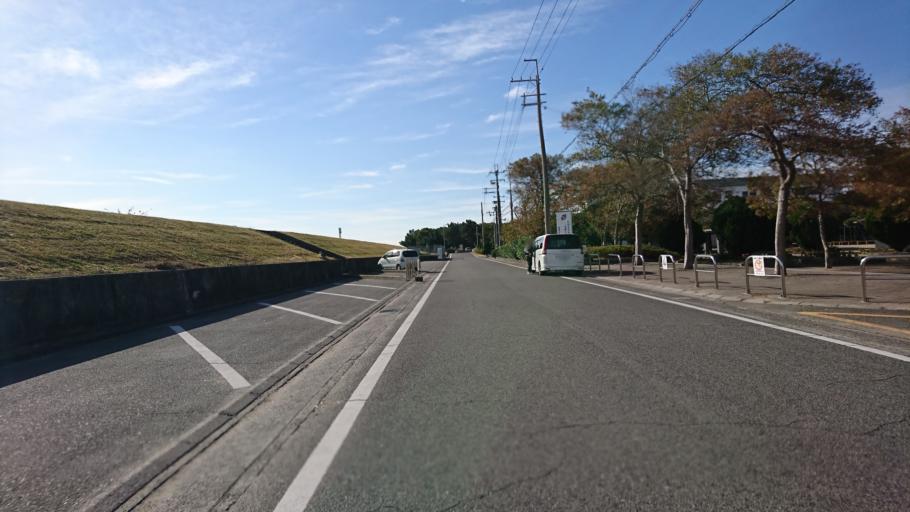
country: JP
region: Hyogo
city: Kakogawacho-honmachi
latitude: 34.7360
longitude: 134.8045
